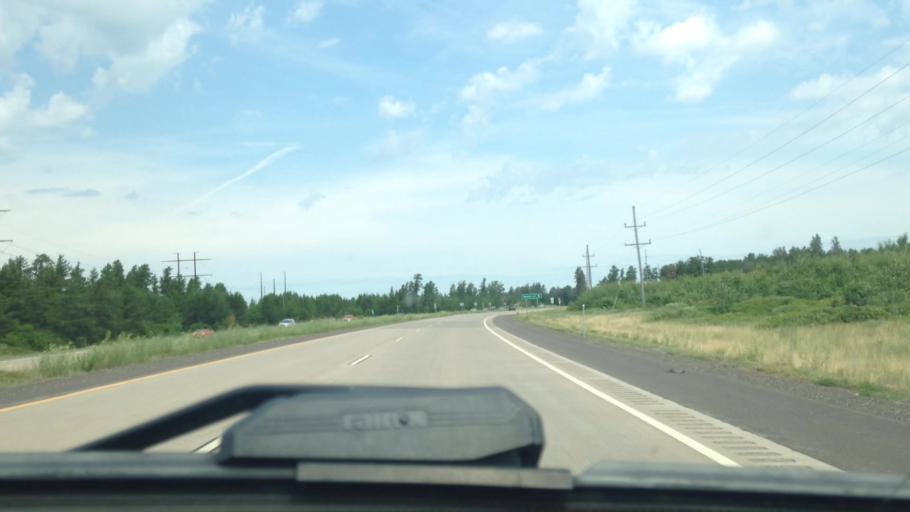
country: US
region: Wisconsin
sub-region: Douglas County
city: Lake Nebagamon
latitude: 46.2851
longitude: -91.8106
